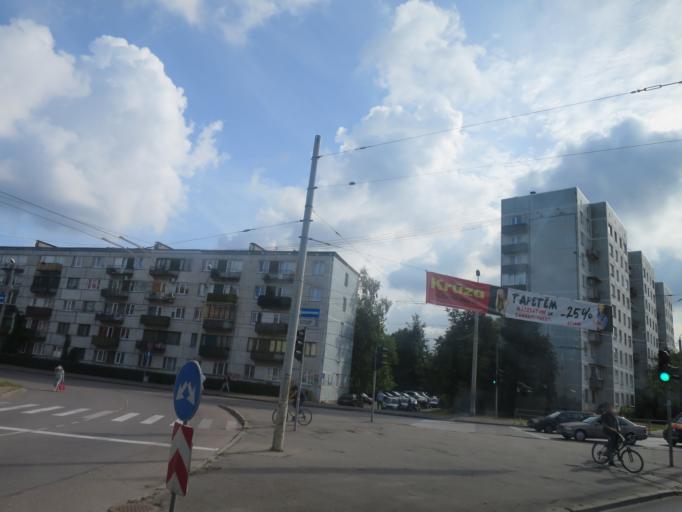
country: LV
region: Riga
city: Riga
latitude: 56.9605
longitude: 24.1750
